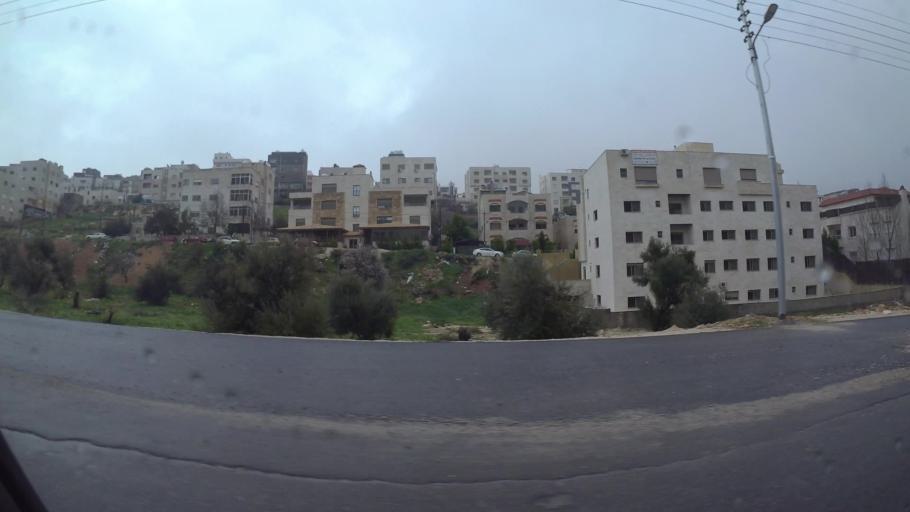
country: JO
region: Amman
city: Al Jubayhah
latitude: 32.0174
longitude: 35.8346
